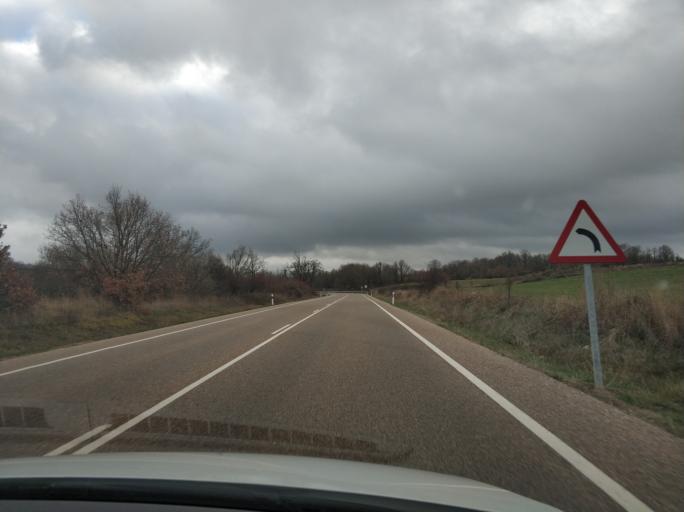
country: ES
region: Castille and Leon
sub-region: Provincia de Segovia
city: Riaza
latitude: 41.3025
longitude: -3.4778
